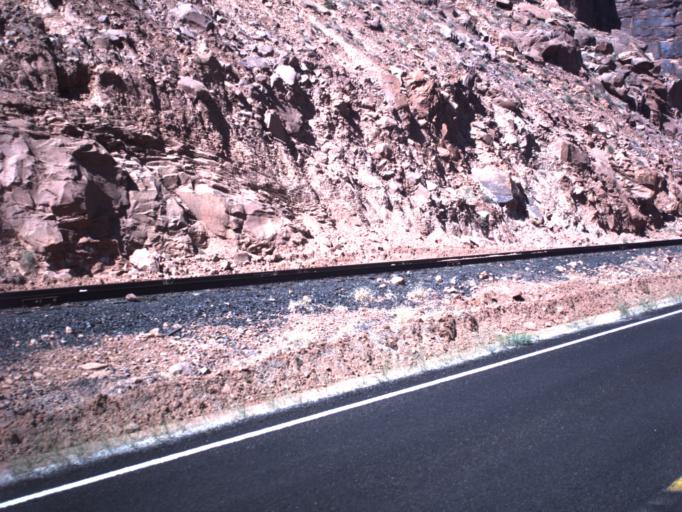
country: US
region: Utah
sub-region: Grand County
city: Moab
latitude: 38.5695
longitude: -109.6569
